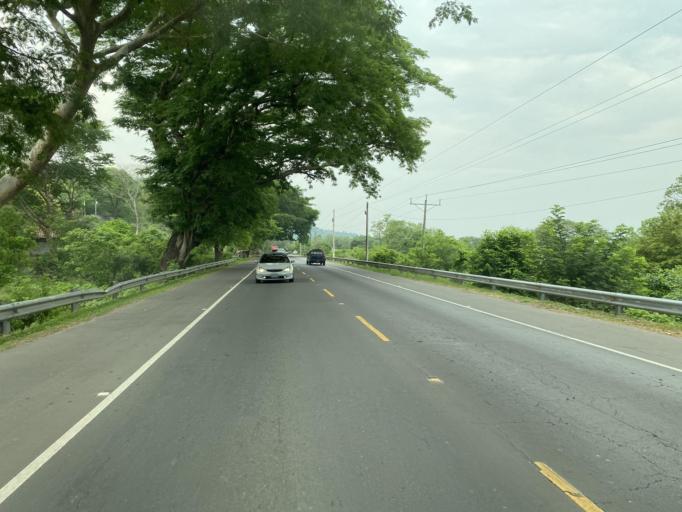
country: SV
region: Usulutan
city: Jucuaran
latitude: 13.3515
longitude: -88.2351
